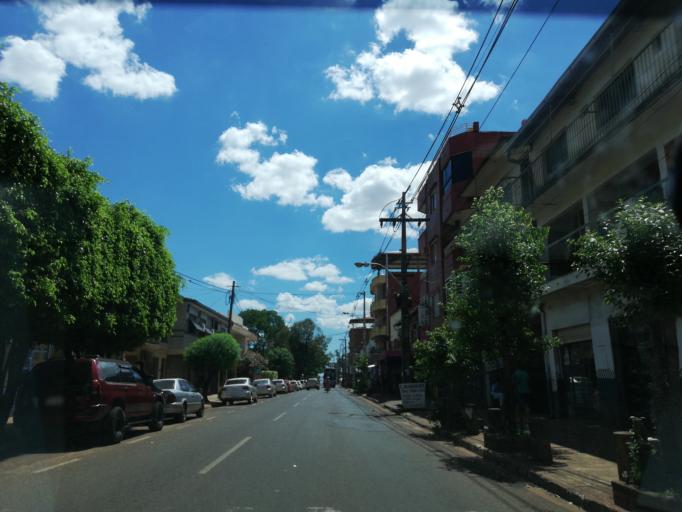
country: PY
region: Itapua
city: Encarnacion
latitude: -27.3407
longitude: -55.8624
